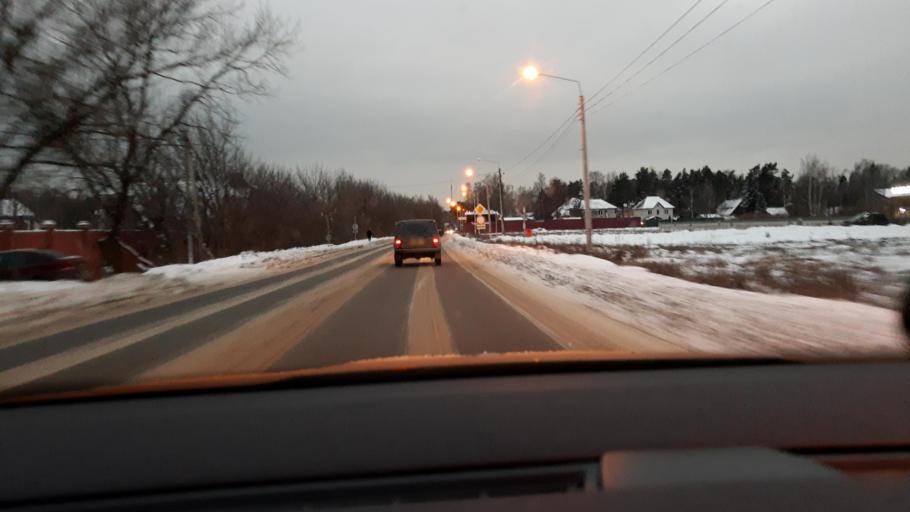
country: RU
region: Moskovskaya
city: Tomilino
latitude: 55.6466
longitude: 37.9542
